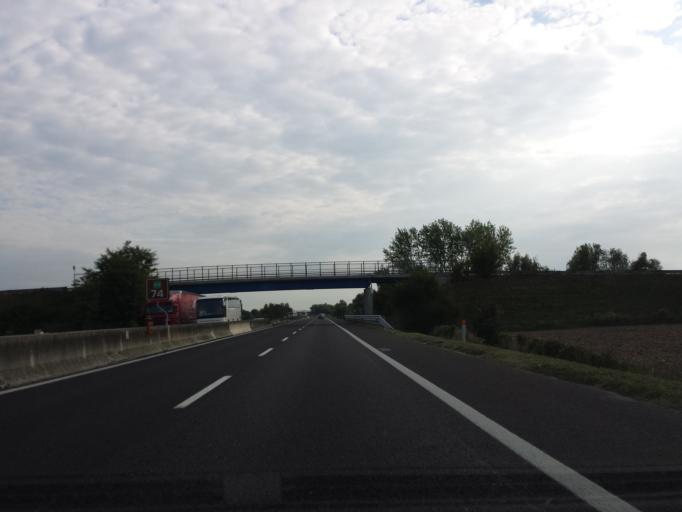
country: IT
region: Veneto
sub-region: Provincia di Padova
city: Pozzonovo
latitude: 45.2051
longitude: 11.7746
